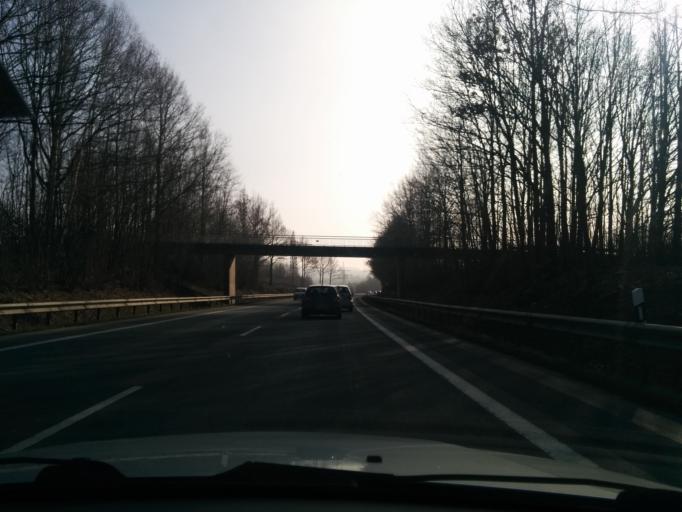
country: DE
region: North Rhine-Westphalia
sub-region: Regierungsbezirk Detmold
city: Blomberg
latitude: 51.9330
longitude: 9.0865
